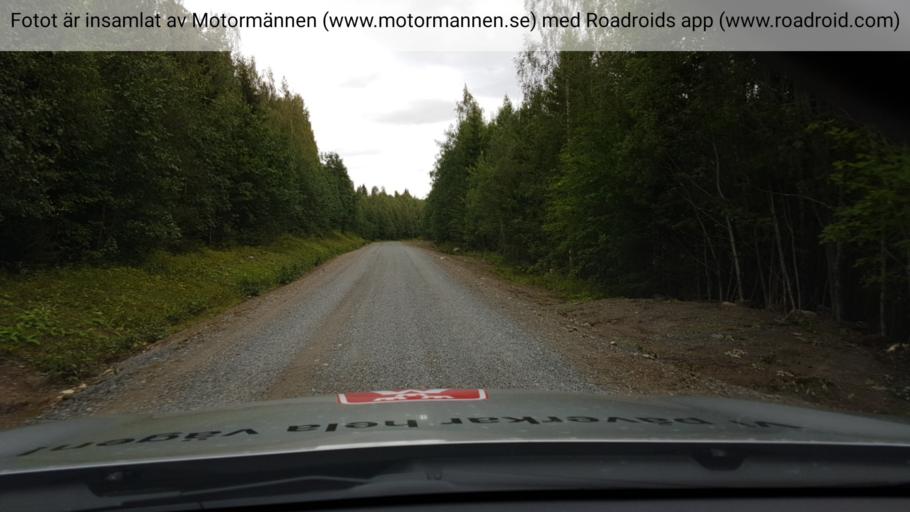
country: SE
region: Jaemtland
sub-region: Ragunda Kommun
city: Hammarstrand
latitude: 62.8876
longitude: 16.0634
